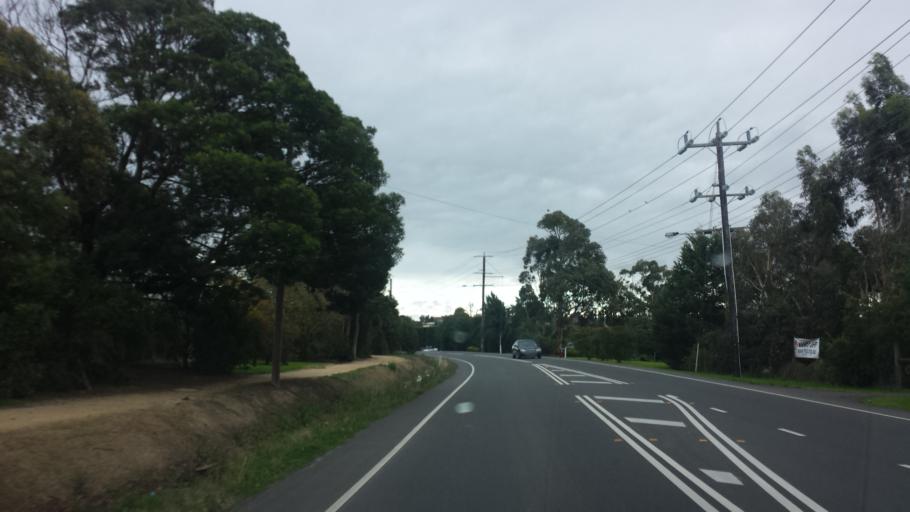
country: AU
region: Victoria
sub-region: Casey
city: Endeavour Hills
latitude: -37.9896
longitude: 145.2826
